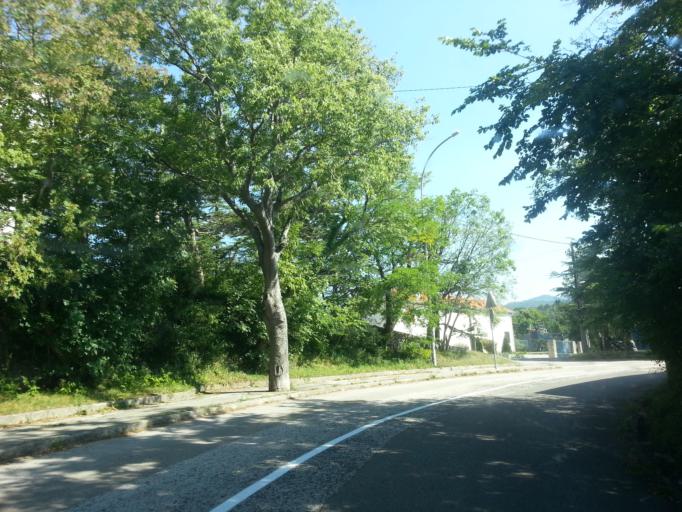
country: HR
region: Primorsko-Goranska
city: Kraljevica
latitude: 45.2754
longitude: 14.5652
